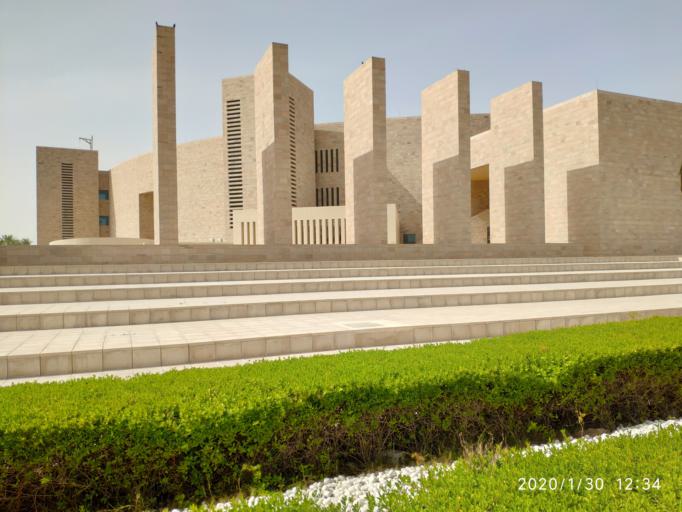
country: QA
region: Baladiyat ar Rayyan
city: Ar Rayyan
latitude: 25.3157
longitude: 51.4399
